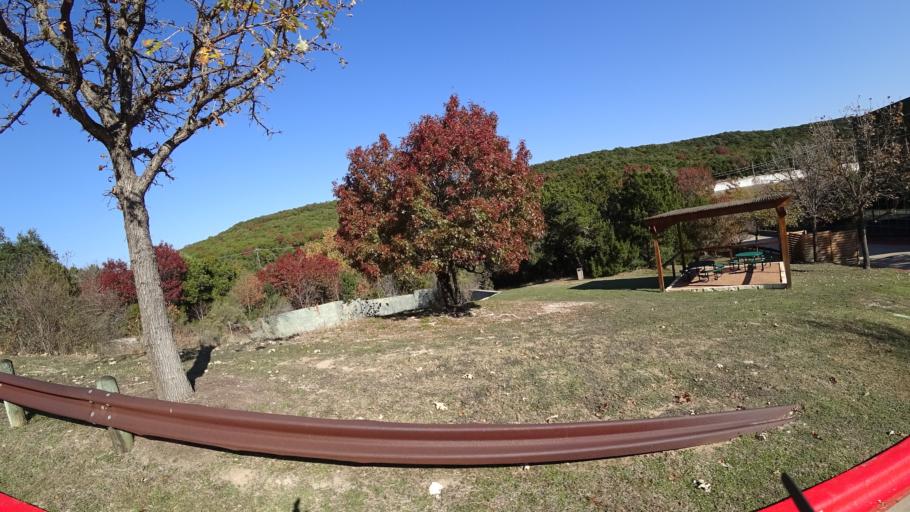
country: US
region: Texas
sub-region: Williamson County
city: Jollyville
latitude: 30.3812
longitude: -97.8147
